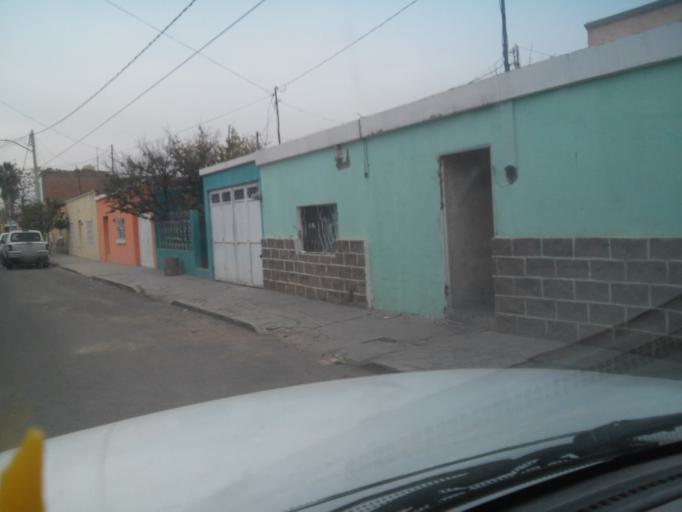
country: MX
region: Durango
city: Victoria de Durango
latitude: 24.0365
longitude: -104.6832
